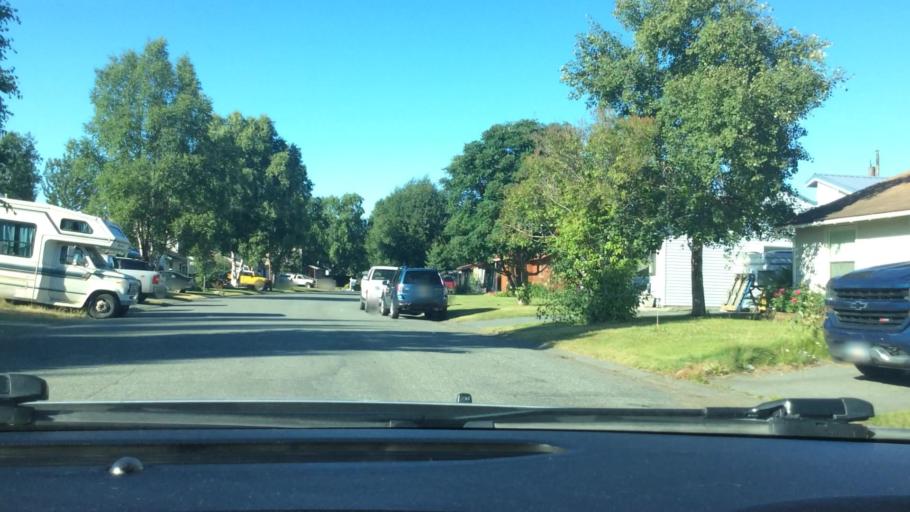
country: US
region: Alaska
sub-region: Anchorage Municipality
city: Anchorage
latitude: 61.2059
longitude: -149.7676
